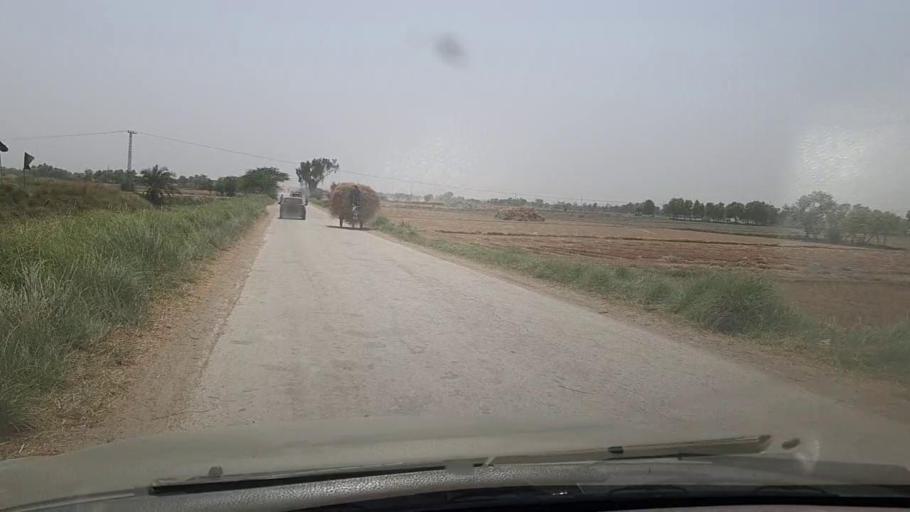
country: PK
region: Sindh
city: Kambar
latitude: 27.6163
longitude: 68.0191
